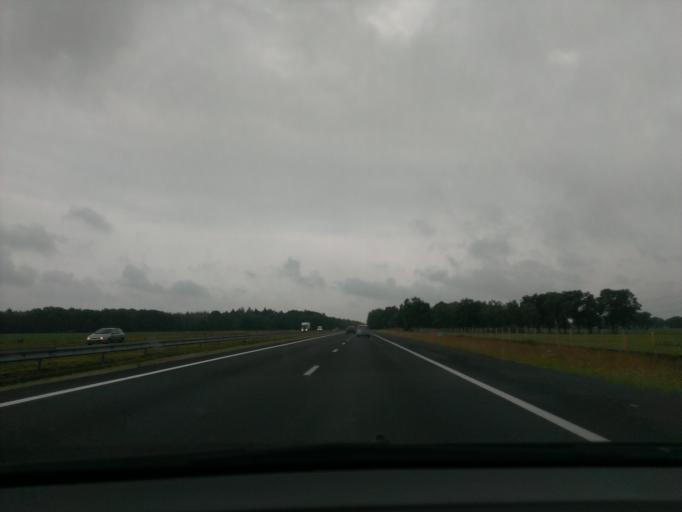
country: NL
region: Drenthe
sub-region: Gemeente Assen
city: Assen
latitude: 52.9335
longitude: 6.5364
